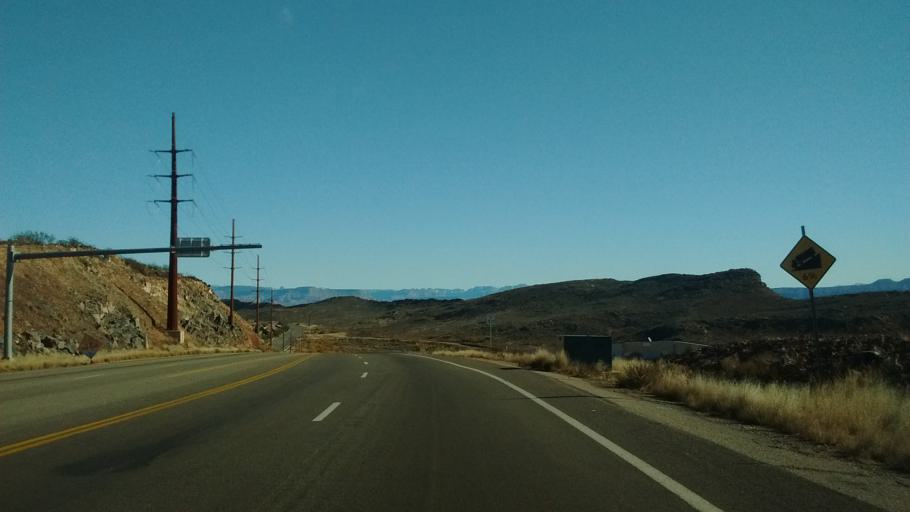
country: US
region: Utah
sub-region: Washington County
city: Washington
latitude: 37.1385
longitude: -113.4683
